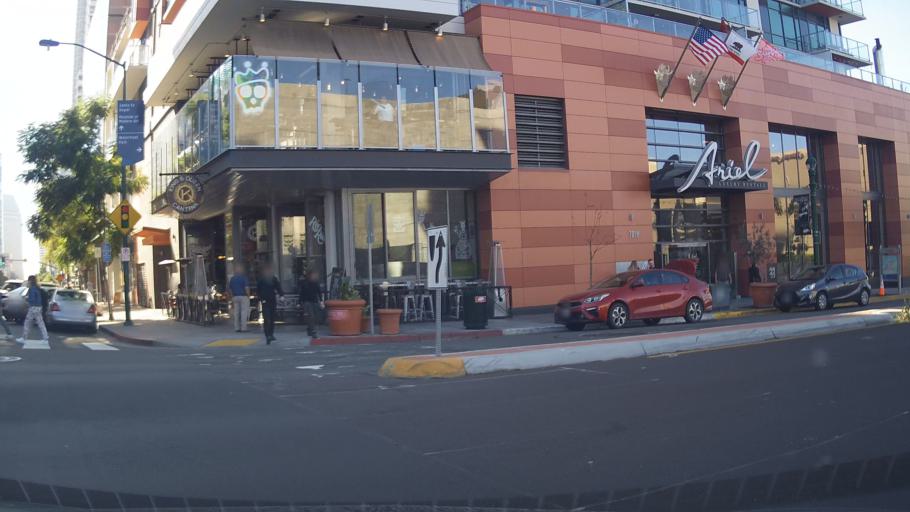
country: US
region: California
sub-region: San Diego County
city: San Diego
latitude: 32.7210
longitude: -117.1692
